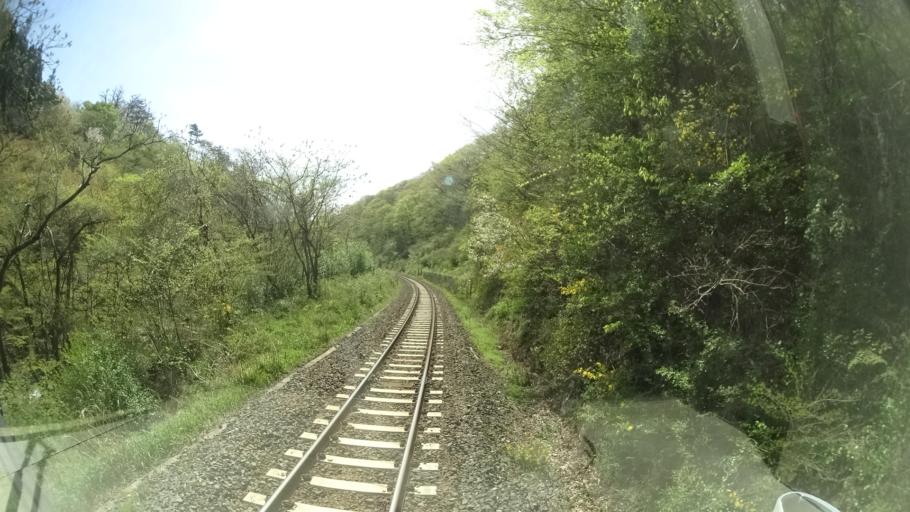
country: JP
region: Iwate
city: Ofunato
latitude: 38.9129
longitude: 141.5084
